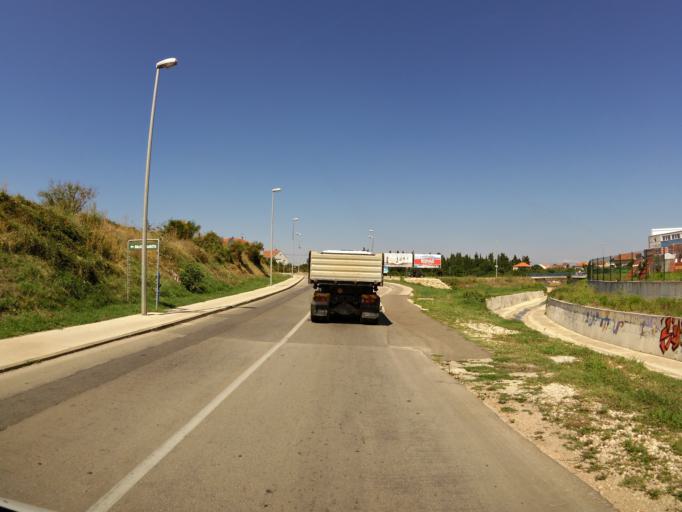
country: HR
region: Zadarska
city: Zadar
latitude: 44.1005
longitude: 15.2558
